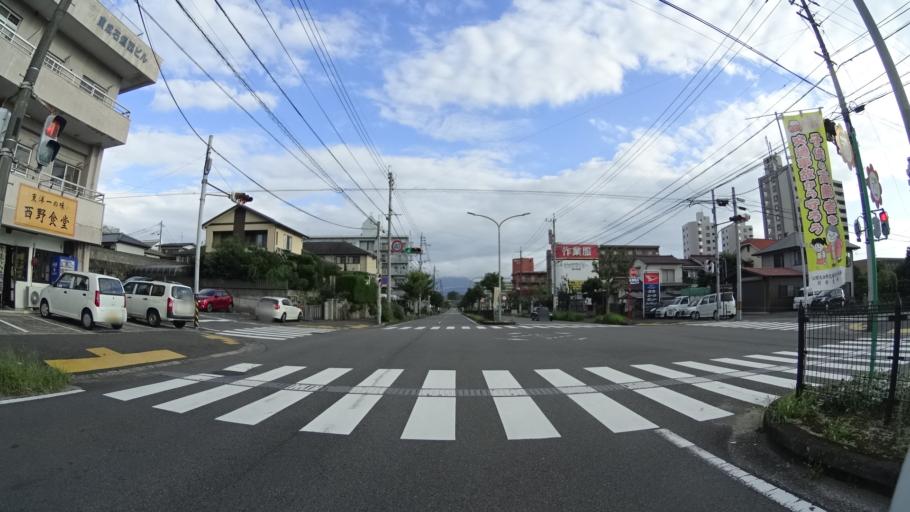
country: JP
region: Oita
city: Beppu
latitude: 33.3008
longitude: 131.4950
